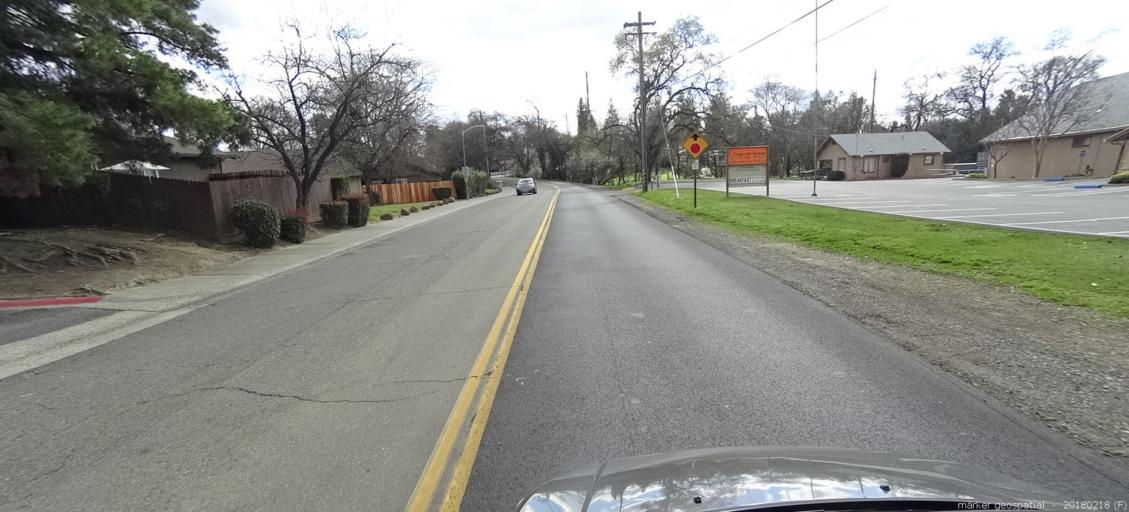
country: US
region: California
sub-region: Sacramento County
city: Orangevale
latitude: 38.6719
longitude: -121.2072
